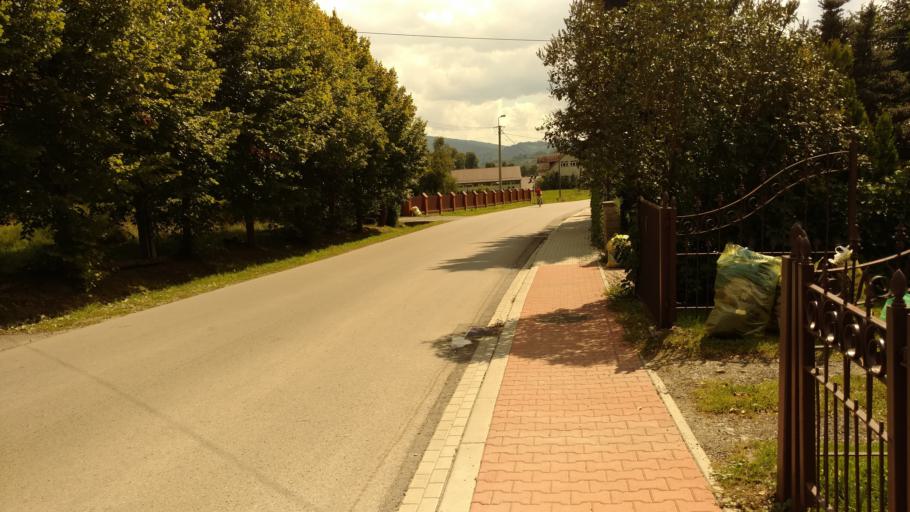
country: PL
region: Lesser Poland Voivodeship
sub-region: Powiat myslenicki
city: Skomielna Czarna
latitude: 49.7304
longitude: 19.8292
